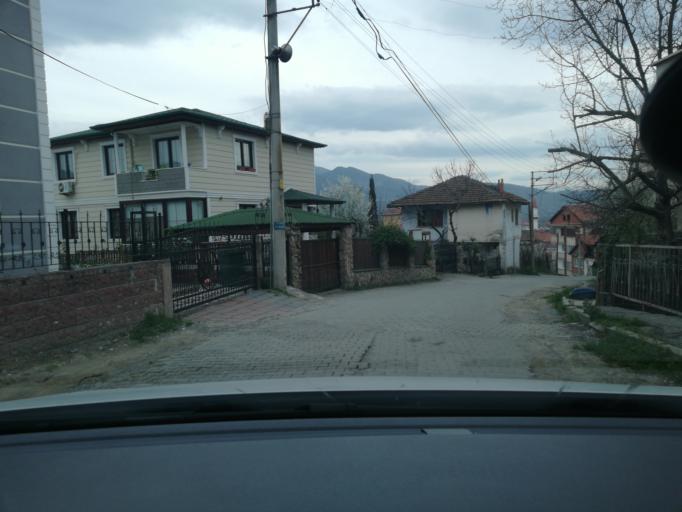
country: TR
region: Zonguldak
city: Gokcebey
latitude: 41.3086
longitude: 32.1415
